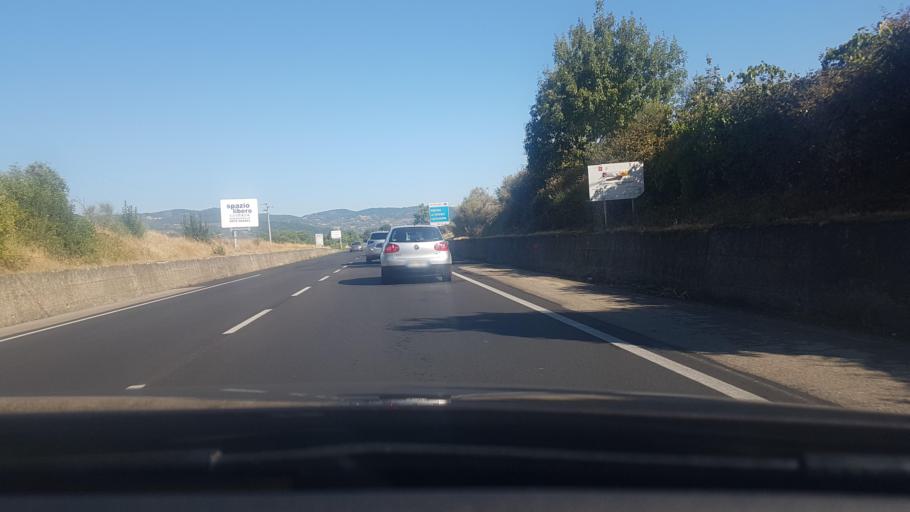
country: IT
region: Tuscany
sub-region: Province of Arezzo
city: Giovi-Ponte alla Chiassa
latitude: 43.5402
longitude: 11.8640
